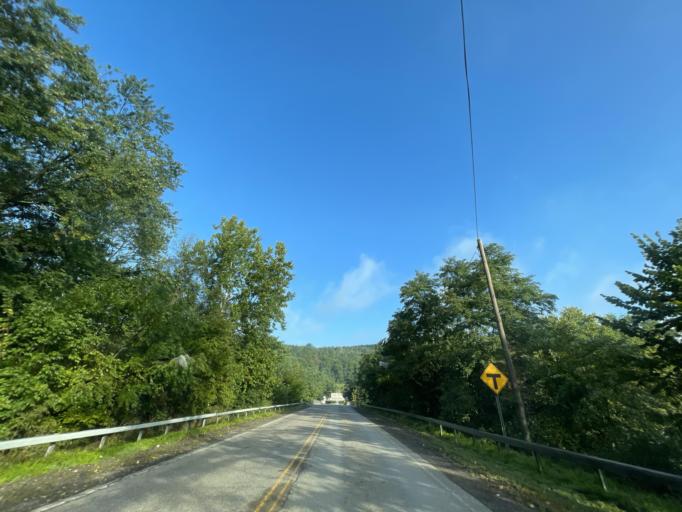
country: US
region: New York
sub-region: Chenango County
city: Greene
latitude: 42.3635
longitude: -75.6800
